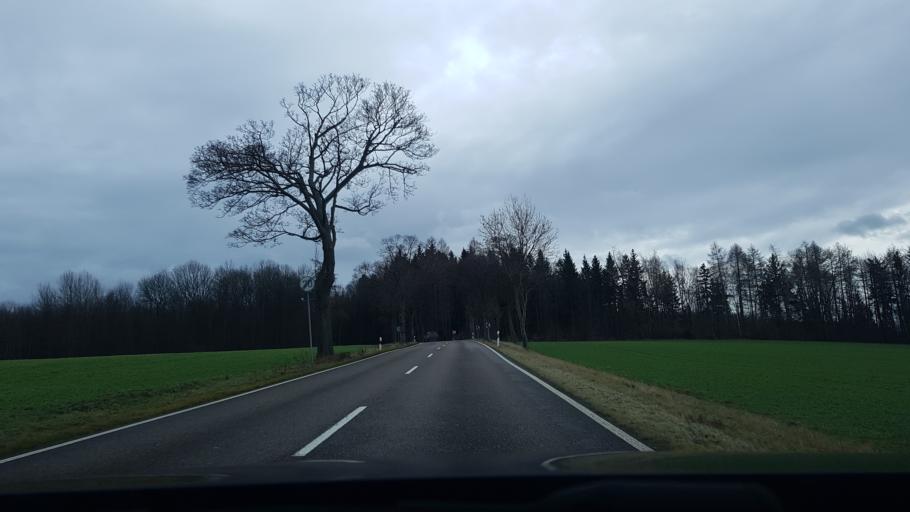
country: DE
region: Saxony
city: Dohma
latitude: 50.8545
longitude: 13.9552
